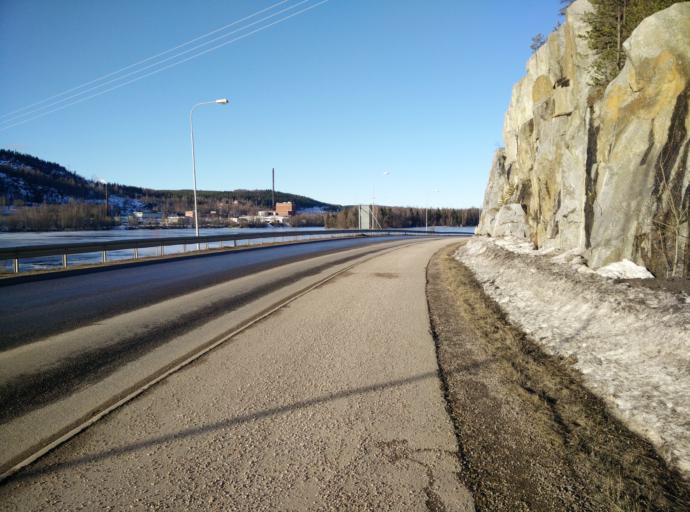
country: SE
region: Vaesternorrland
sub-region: Sundsvalls Kommun
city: Skottsund
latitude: 62.3023
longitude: 17.3846
